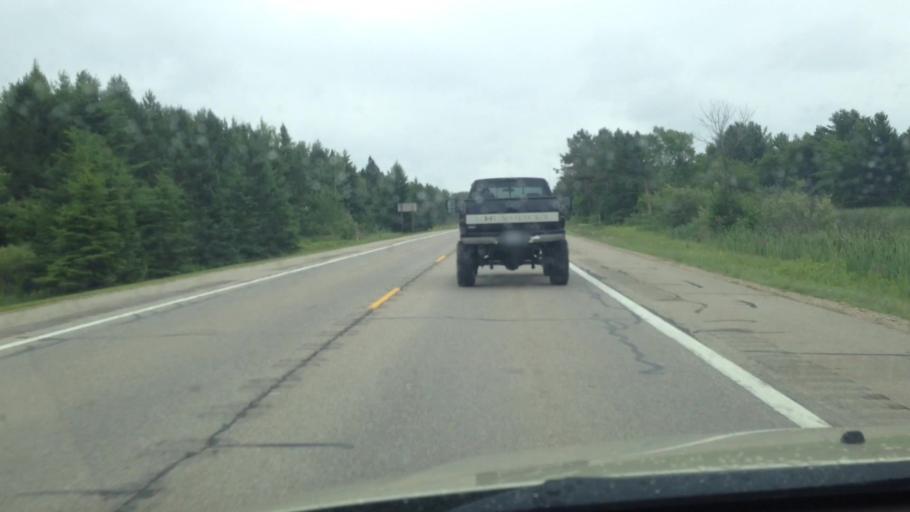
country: US
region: Michigan
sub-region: Schoolcraft County
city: Manistique
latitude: 45.8960
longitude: -86.5506
